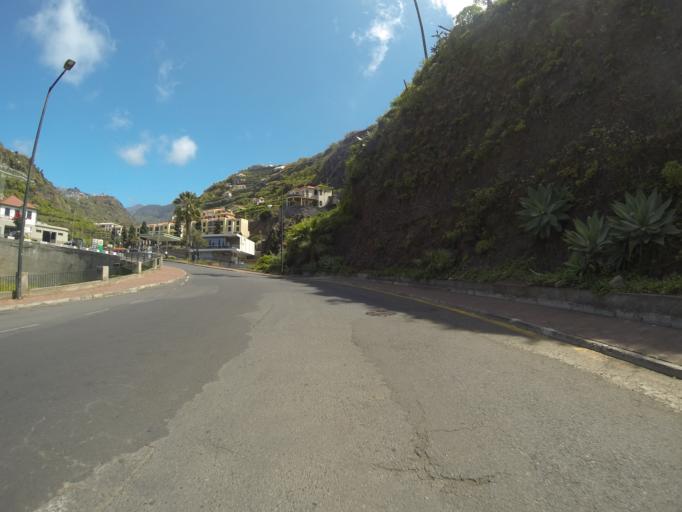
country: PT
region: Madeira
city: Ponta do Sol
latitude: 32.6810
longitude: -17.1018
